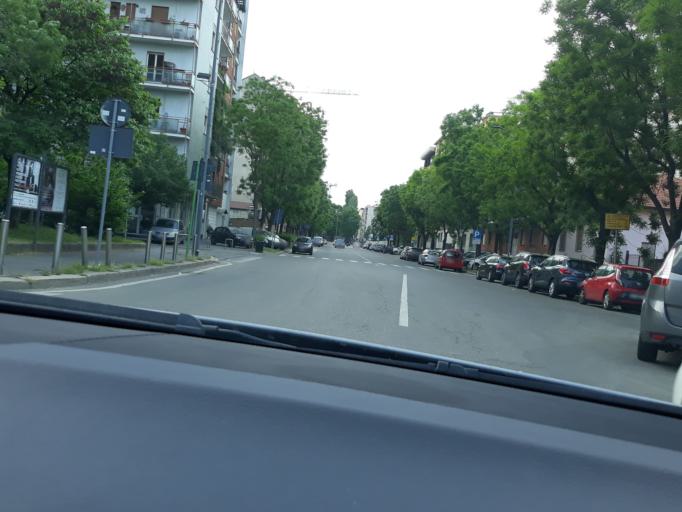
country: IT
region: Lombardy
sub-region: Citta metropolitana di Milano
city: Milano
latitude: 45.4897
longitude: 9.1700
